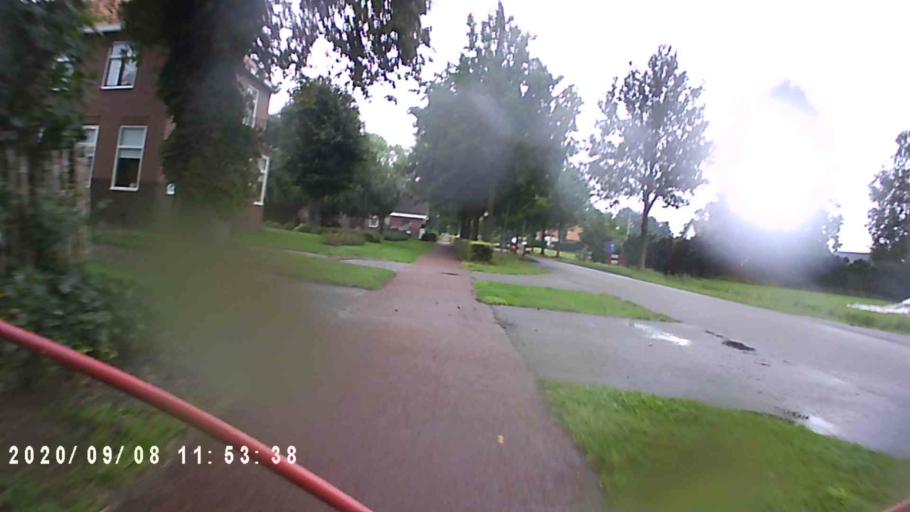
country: NL
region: Groningen
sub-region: Gemeente Hoogezand-Sappemeer
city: Sappemeer
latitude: 53.1203
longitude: 6.8170
